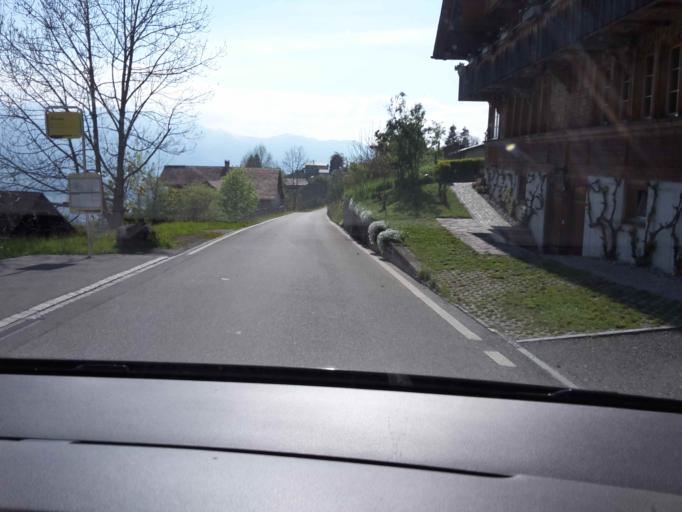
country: CH
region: Bern
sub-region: Thun District
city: Hilterfingen
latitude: 46.7633
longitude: 7.6796
